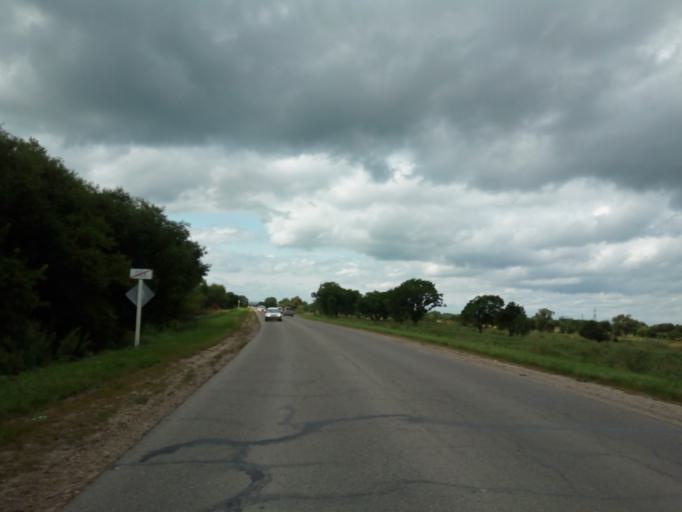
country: RU
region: Primorskiy
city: Dal'nerechensk
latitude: 45.9465
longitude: 133.7998
